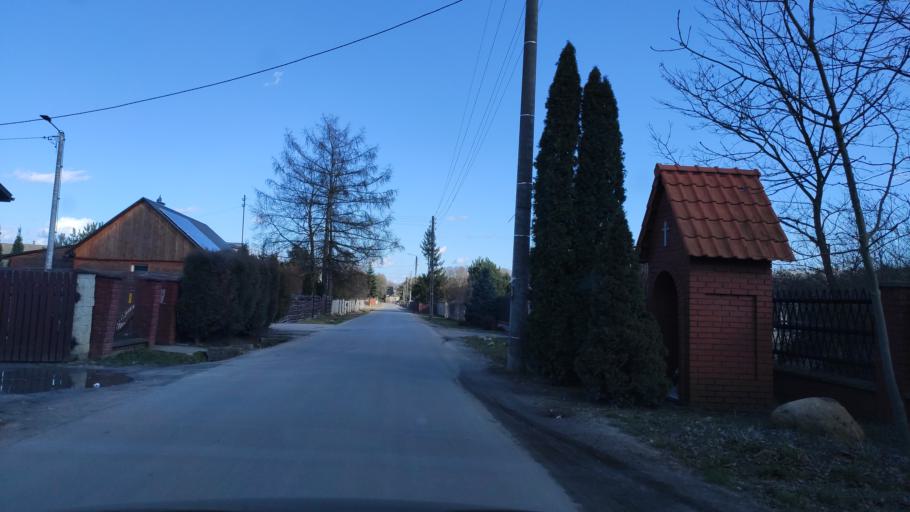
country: PL
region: Masovian Voivodeship
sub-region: Powiat radomski
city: Jedlnia-Letnisko
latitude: 51.4395
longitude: 21.3012
